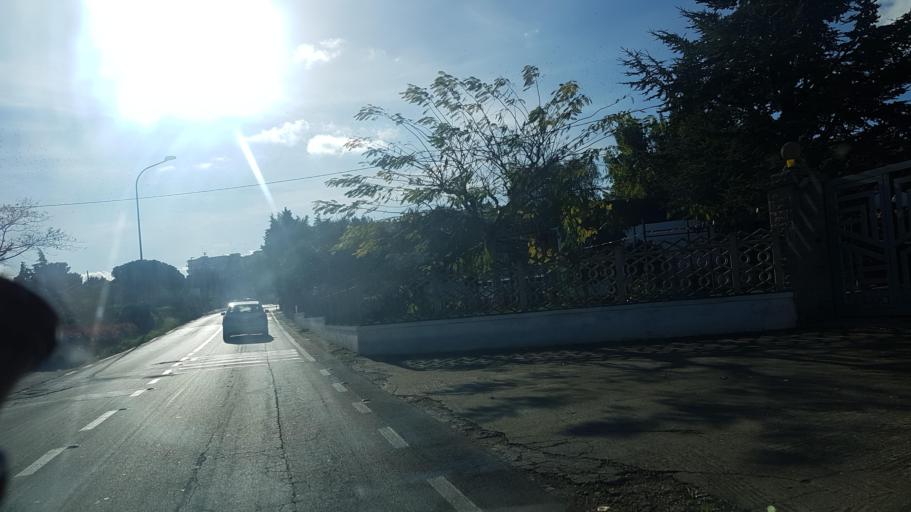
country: IT
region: Apulia
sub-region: Provincia di Brindisi
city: Ceglie Messapica
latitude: 40.6504
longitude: 17.5231
